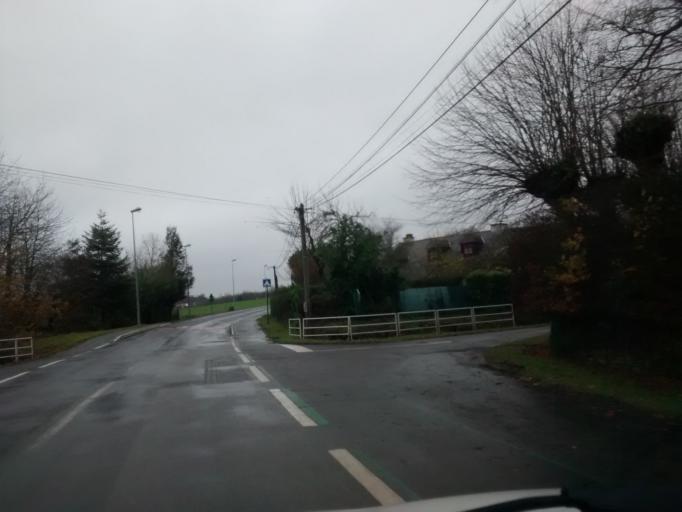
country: FR
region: Brittany
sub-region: Departement d'Ille-et-Vilaine
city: Cesson-Sevigne
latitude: 48.1083
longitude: -1.5814
